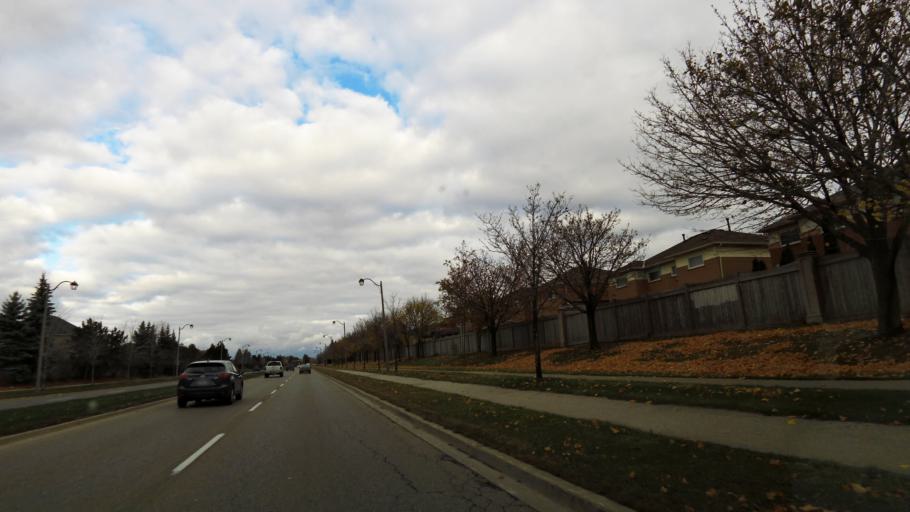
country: CA
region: Ontario
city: Brampton
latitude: 43.7470
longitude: -79.7669
